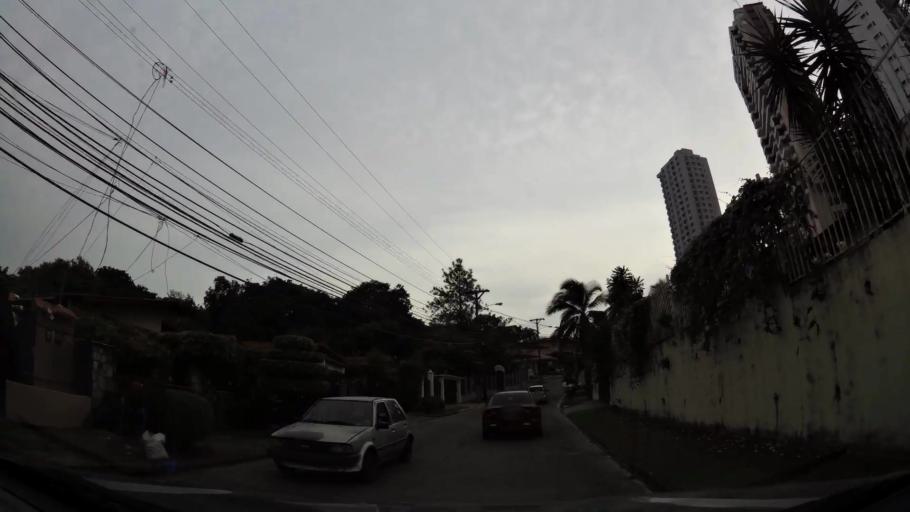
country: PA
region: Panama
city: Panama
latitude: 9.0178
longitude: -79.5329
